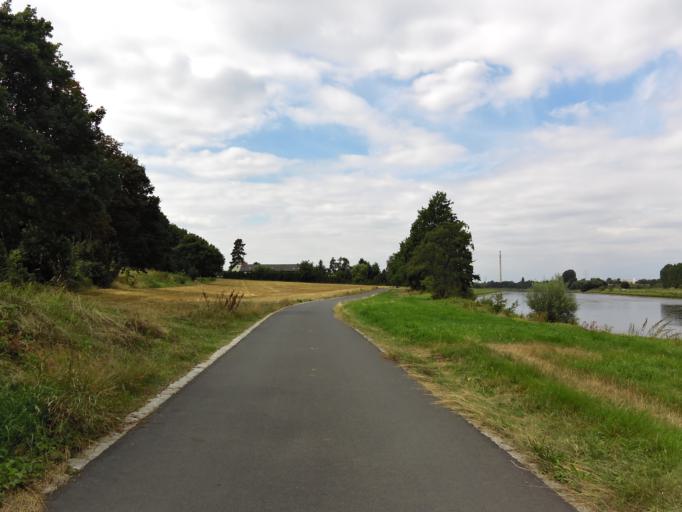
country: DE
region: Saxony
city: Coswig
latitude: 51.0962
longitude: 13.6004
